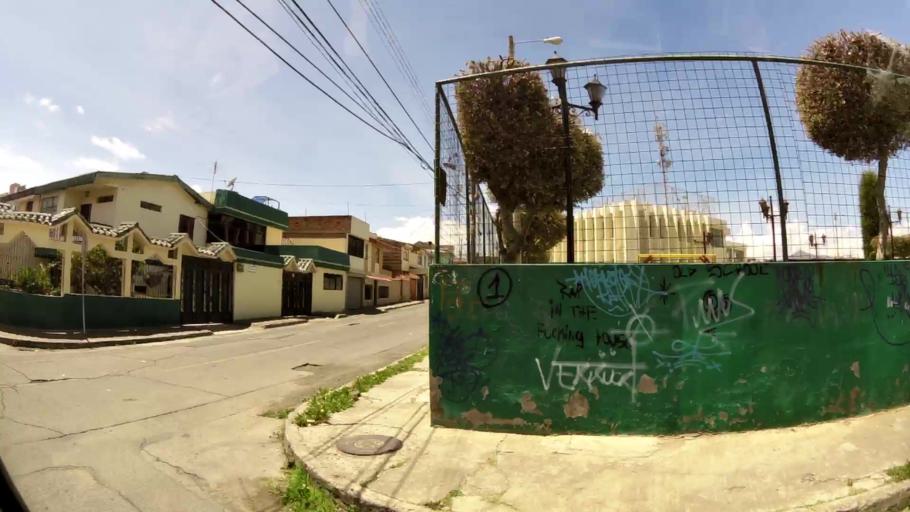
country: EC
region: Chimborazo
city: Riobamba
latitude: -1.6604
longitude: -78.6573
